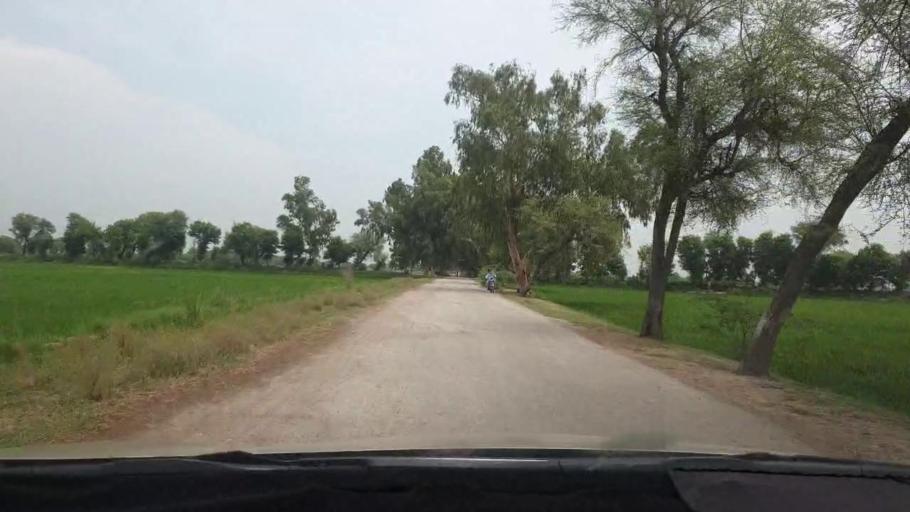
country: PK
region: Sindh
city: Ratodero
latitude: 27.7593
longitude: 68.3182
